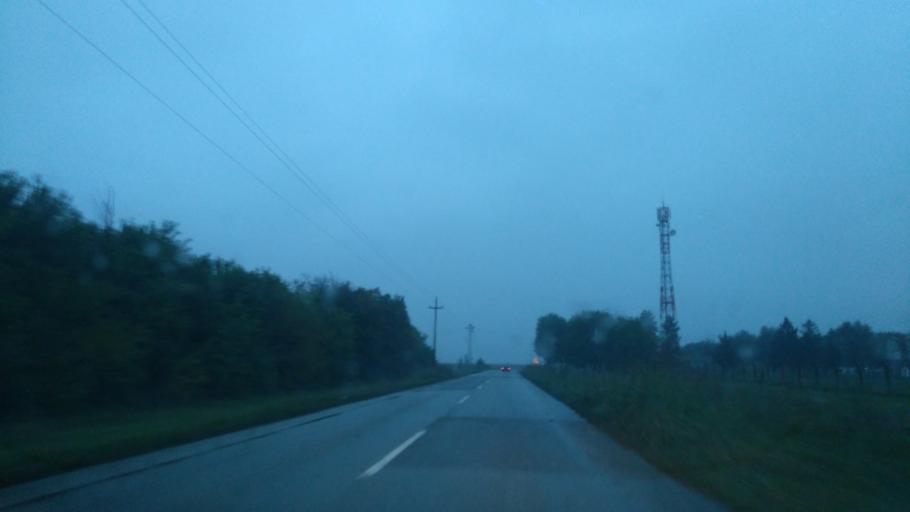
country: RS
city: Backo Petrovo Selo
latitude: 45.7228
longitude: 20.0953
